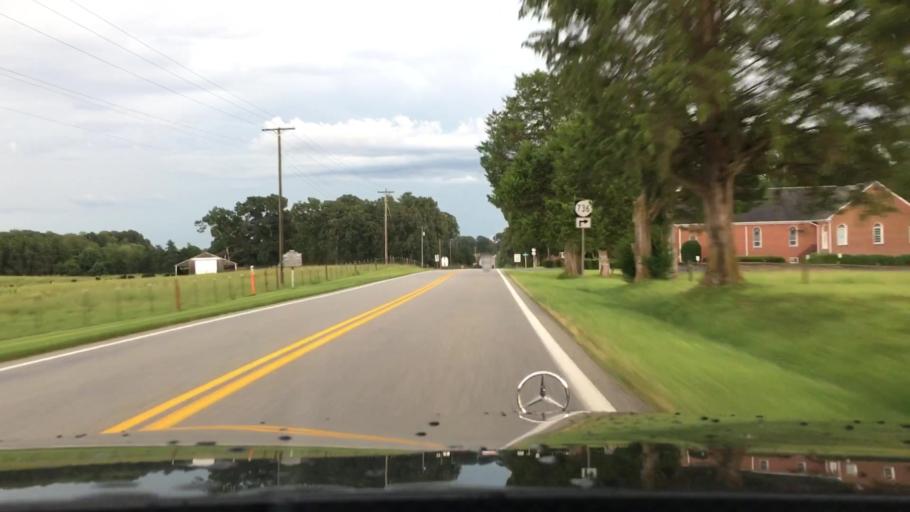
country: US
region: Virginia
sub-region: Amherst County
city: Amherst
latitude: 37.6360
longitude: -79.0218
